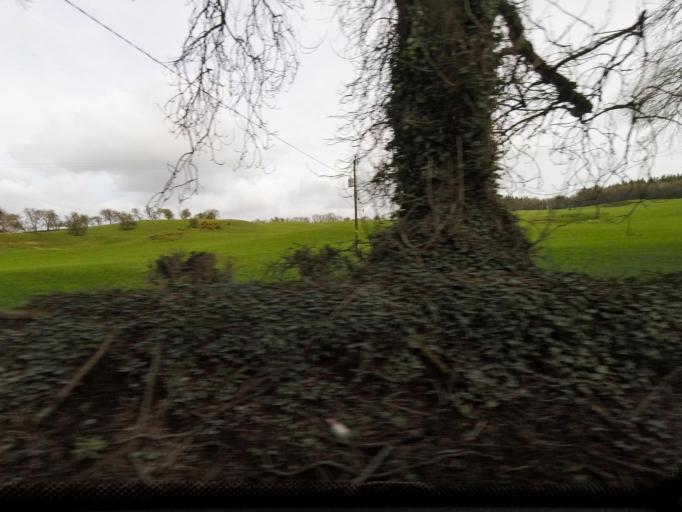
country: IE
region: Leinster
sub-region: Kildare
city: Eadestown
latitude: 53.1877
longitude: -6.5586
